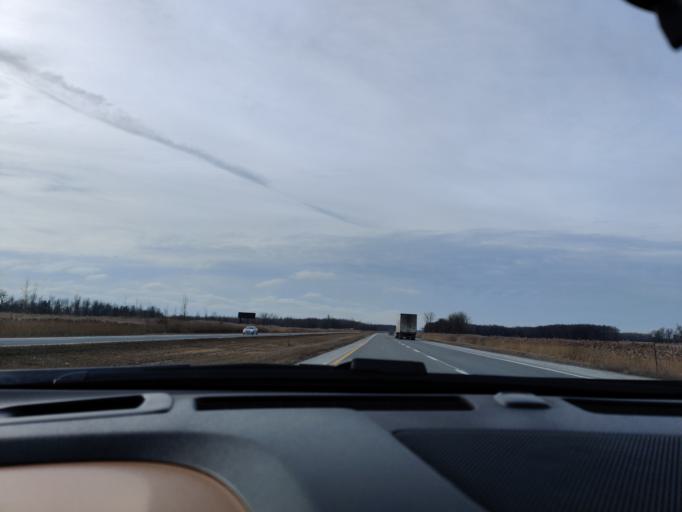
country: CA
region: Quebec
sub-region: Monteregie
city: Les Coteaux
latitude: 45.2510
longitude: -74.2568
